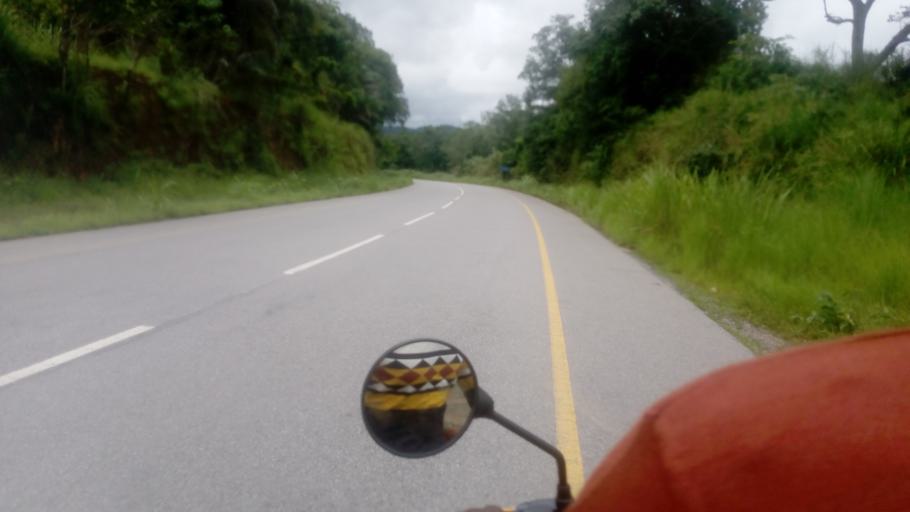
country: SL
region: Northern Province
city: Masaka
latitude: 8.6431
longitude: -11.7413
